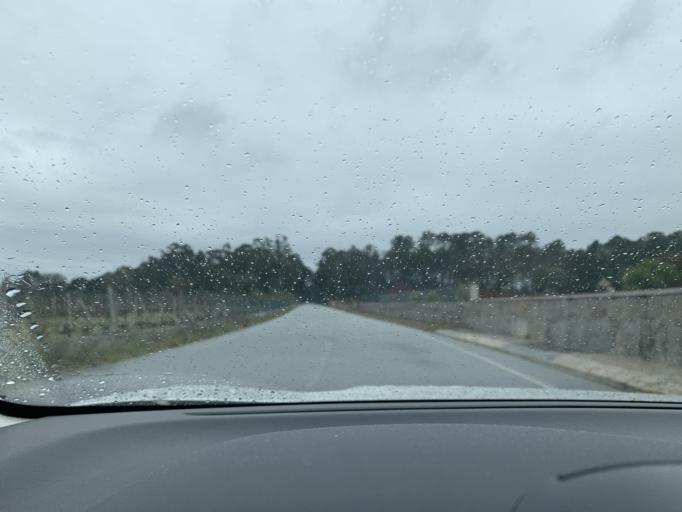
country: PT
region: Viseu
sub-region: Mangualde
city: Mangualde
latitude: 40.5973
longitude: -7.8211
